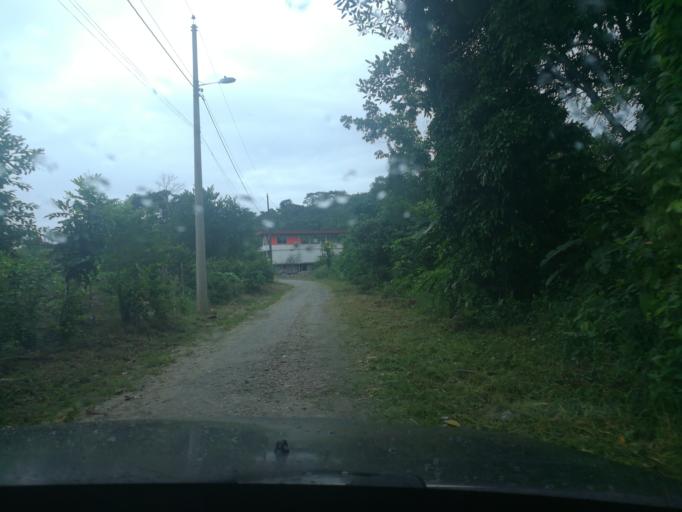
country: EC
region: Napo
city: Tena
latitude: -1.0490
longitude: -77.7976
